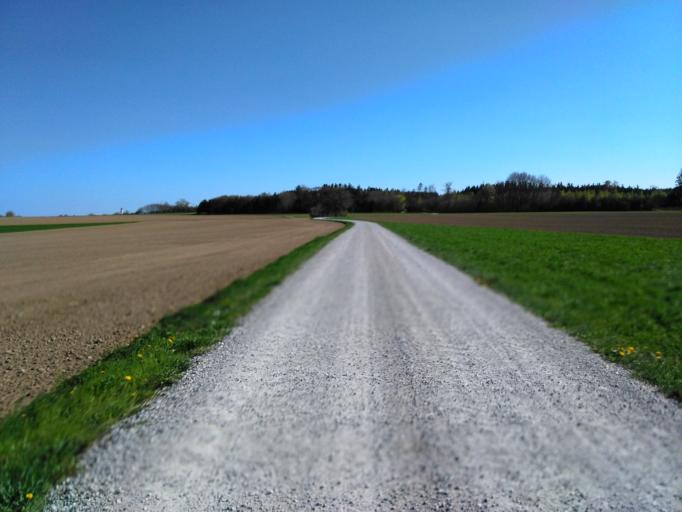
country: DE
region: Bavaria
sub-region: Upper Bavaria
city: Landsberied
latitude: 48.2047
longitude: 11.2034
